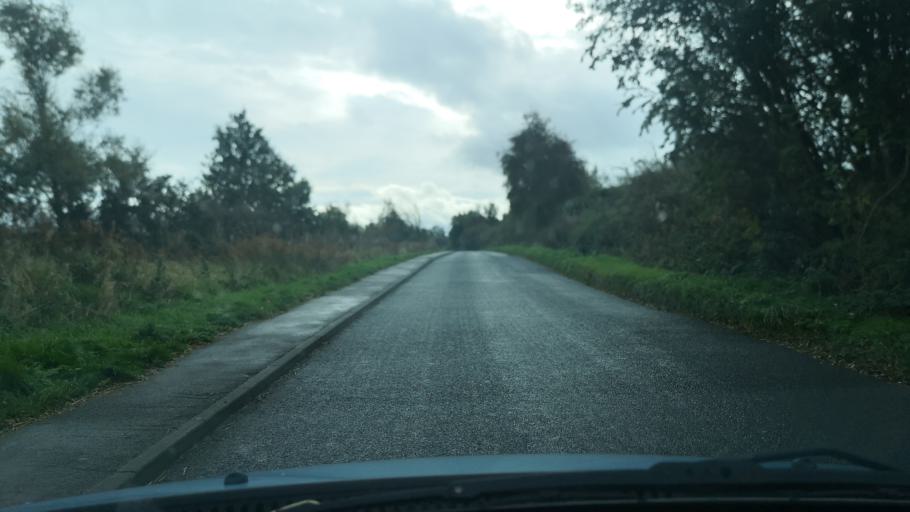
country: GB
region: England
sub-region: City and Borough of Wakefield
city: Sharlston
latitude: 53.6697
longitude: -1.4066
